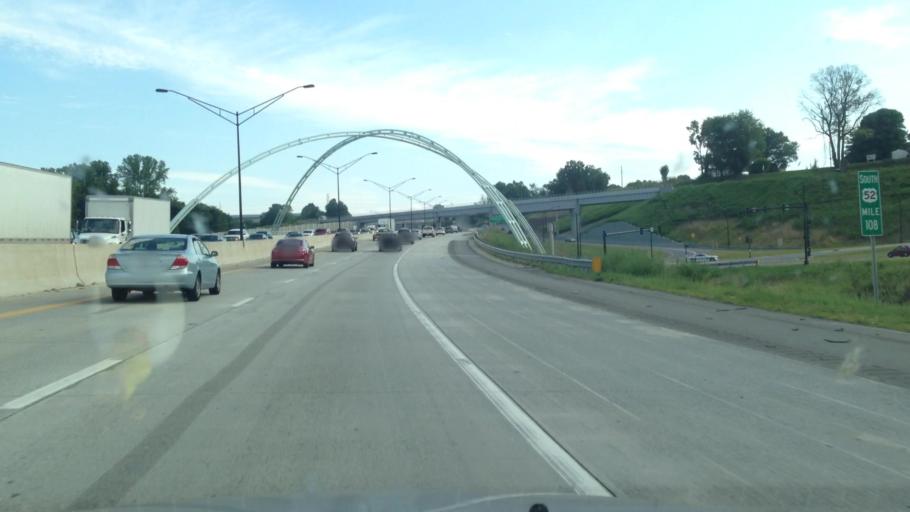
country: US
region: North Carolina
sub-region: Forsyth County
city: Winston-Salem
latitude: 36.0855
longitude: -80.2291
